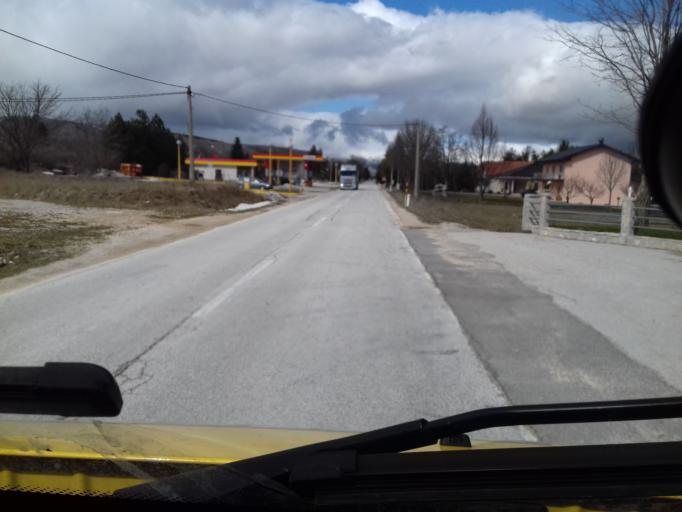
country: BA
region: Federation of Bosnia and Herzegovina
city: Dreznica
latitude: 43.6236
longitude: 17.2560
